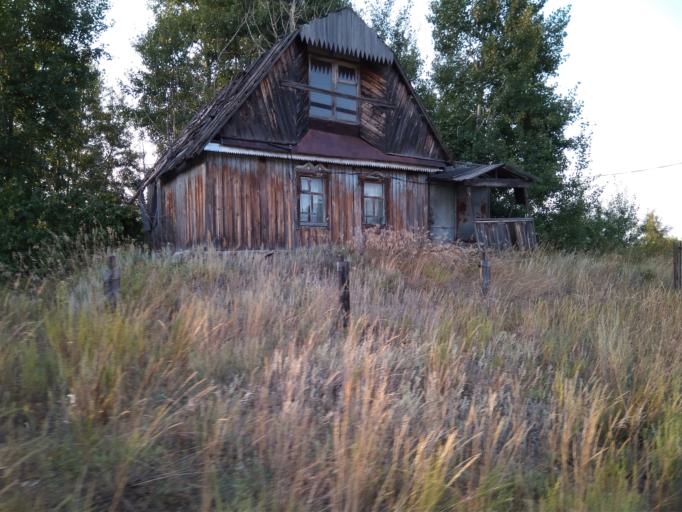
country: RU
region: Ulyanovsk
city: Staraya Mayna
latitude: 54.6449
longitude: 49.0493
